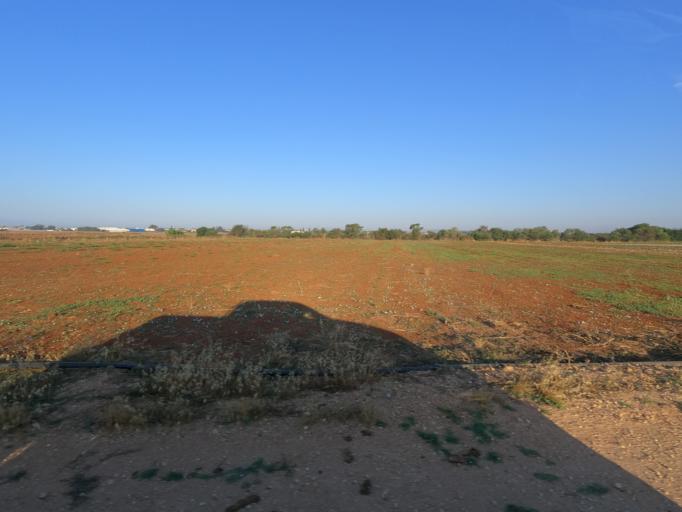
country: CY
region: Ammochostos
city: Achna
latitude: 35.0314
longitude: 33.7913
